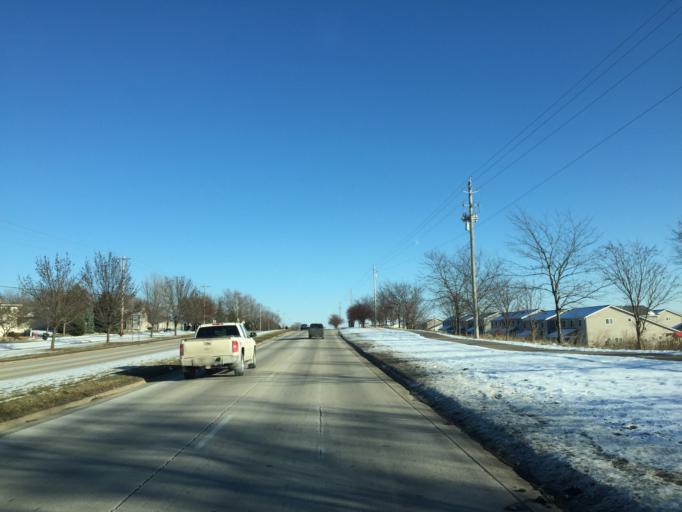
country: US
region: Minnesota
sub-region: Olmsted County
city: Rochester
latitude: 44.0797
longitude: -92.5040
